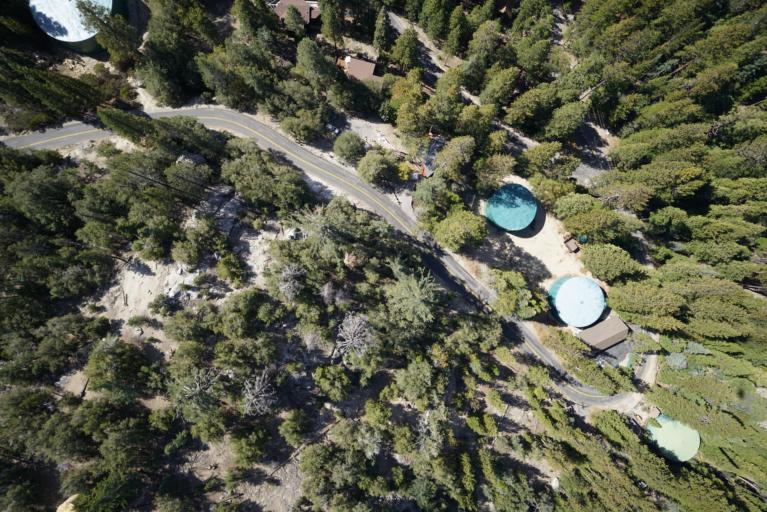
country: US
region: California
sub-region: Riverside County
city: Idyllwild
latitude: 33.7660
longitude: -116.6890
